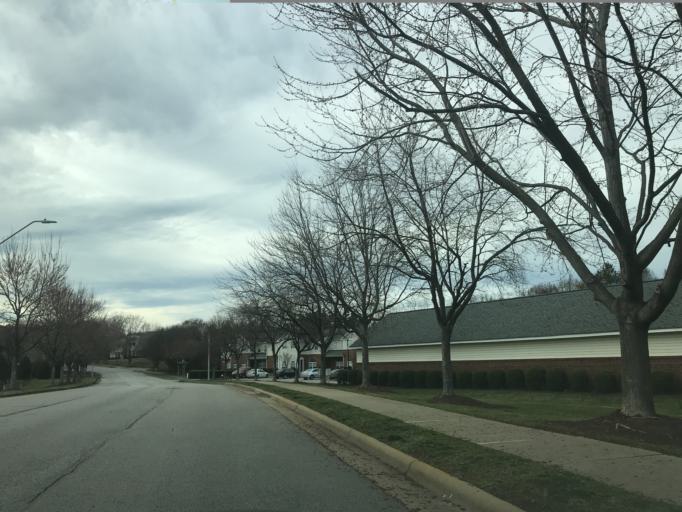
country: US
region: North Carolina
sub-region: Wake County
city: Wake Forest
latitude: 35.9238
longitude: -78.5702
